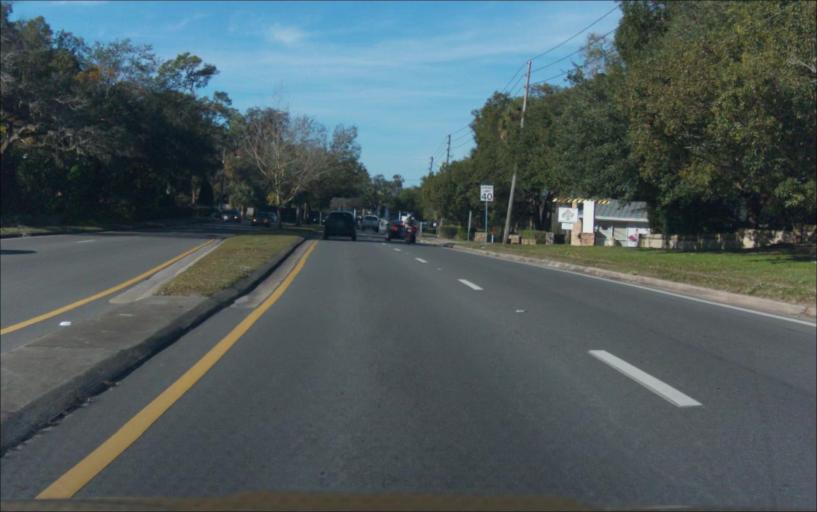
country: US
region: Florida
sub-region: Orange County
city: Maitland
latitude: 28.6318
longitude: -81.3678
